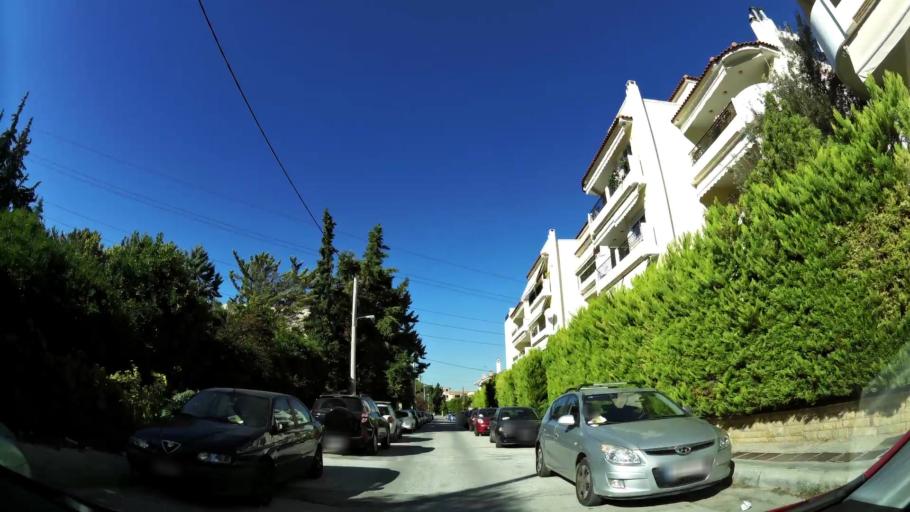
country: GR
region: Attica
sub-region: Nomarchia Anatolikis Attikis
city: Leondarion
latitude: 37.9903
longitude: 23.8473
